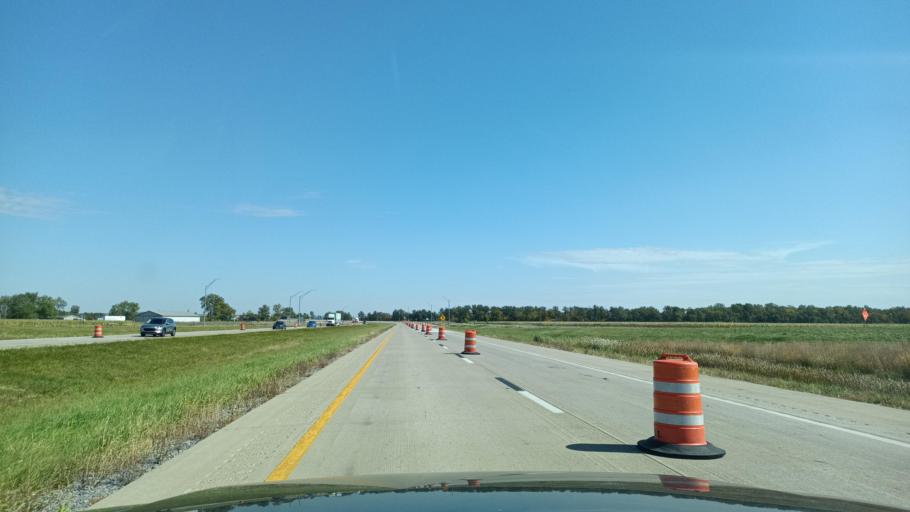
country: US
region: Ohio
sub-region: Paulding County
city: Paulding
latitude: 41.2199
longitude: -84.5812
